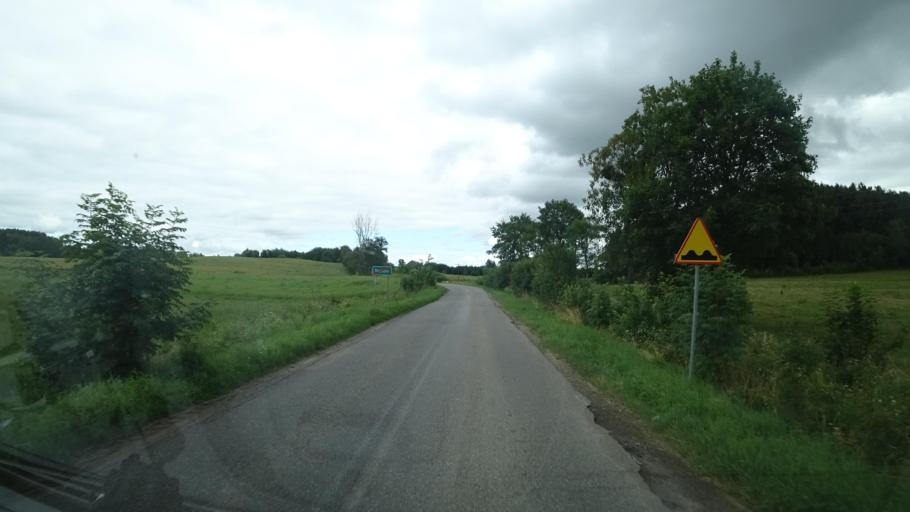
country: PL
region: Podlasie
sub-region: Powiat suwalski
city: Filipow
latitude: 54.2833
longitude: 22.5218
